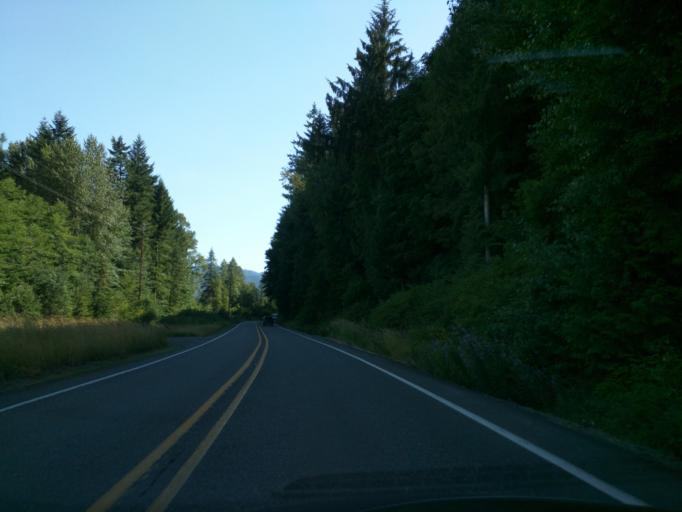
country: US
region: Washington
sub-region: Whatcom County
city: Peaceful Valley
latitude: 48.8624
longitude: -122.1536
